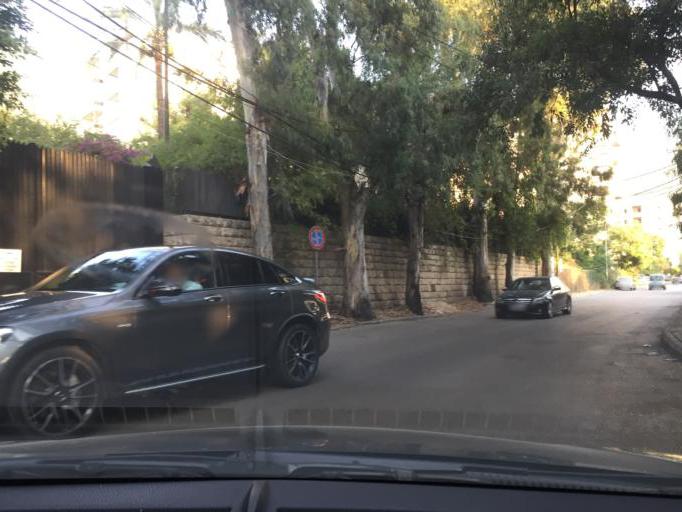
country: LB
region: Mont-Liban
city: Djounie
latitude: 33.9942
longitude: 35.6422
